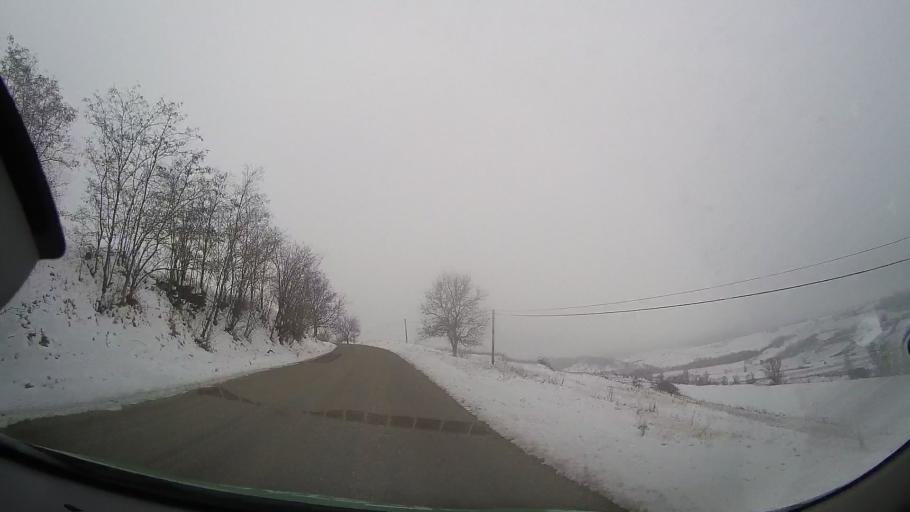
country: RO
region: Bacau
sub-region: Comuna Vultureni
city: Vultureni
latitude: 46.3777
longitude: 27.2760
